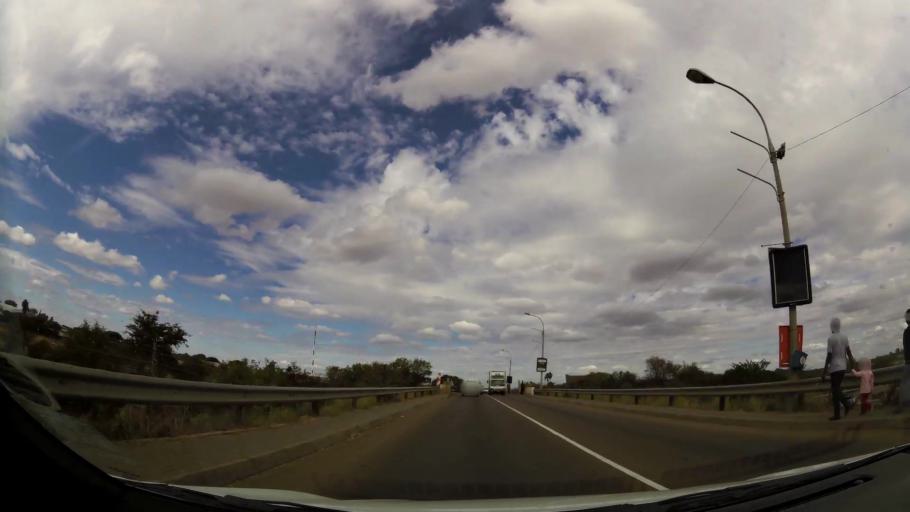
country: ZA
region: Limpopo
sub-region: Waterberg District Municipality
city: Bela-Bela
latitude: -24.8892
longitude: 28.2943
